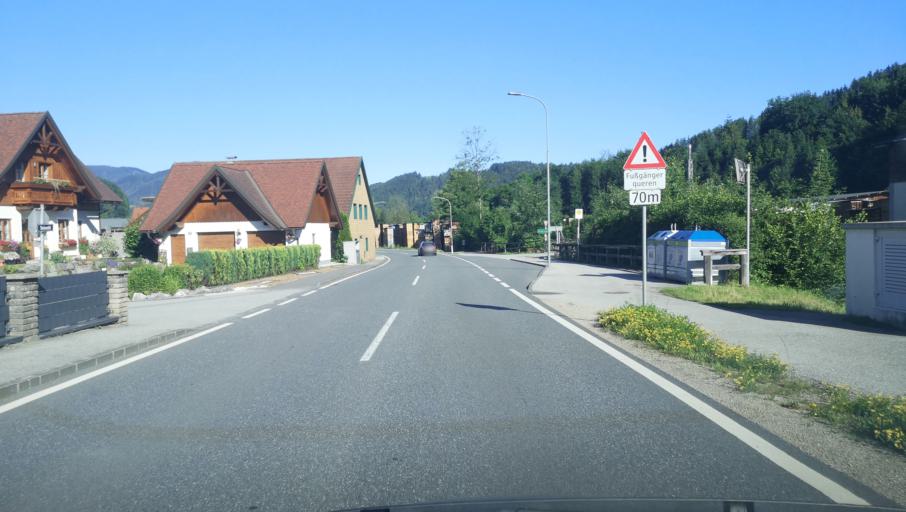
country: AT
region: Lower Austria
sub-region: Politischer Bezirk Amstetten
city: Ybbsitz
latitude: 47.9432
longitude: 14.8333
